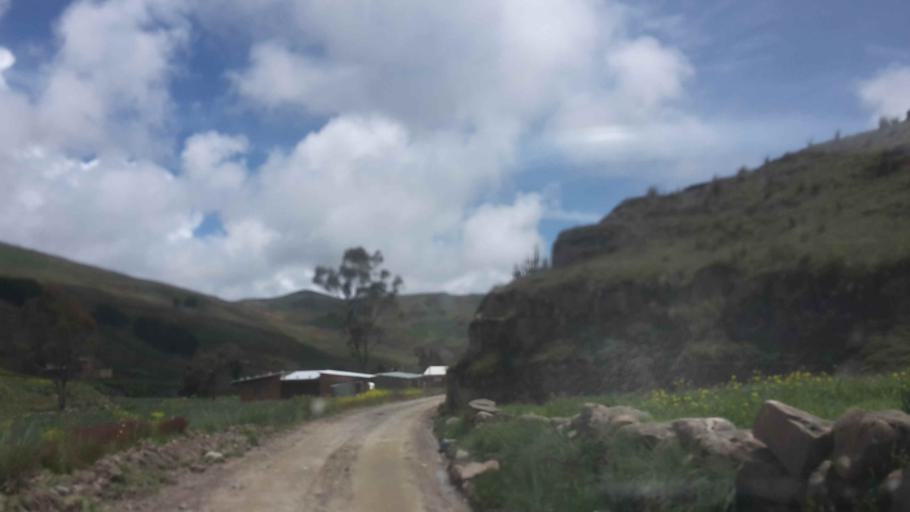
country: BO
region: Cochabamba
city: Cochabamba
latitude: -17.1981
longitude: -66.0833
